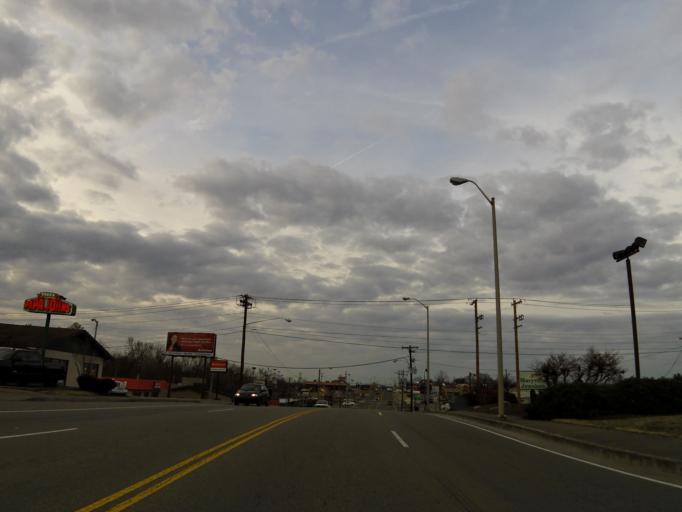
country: US
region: Tennessee
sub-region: Blount County
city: Maryville
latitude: 35.7579
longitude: -83.9741
